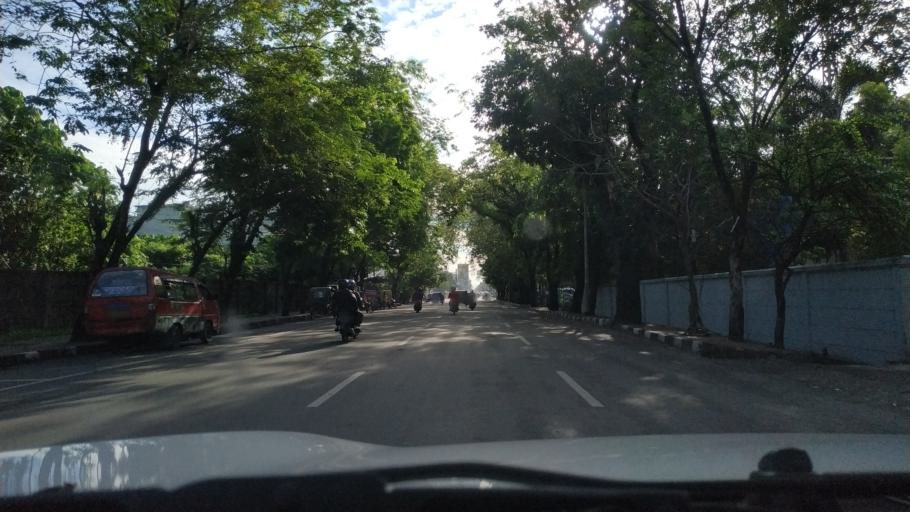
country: ID
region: North Sumatra
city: Medan
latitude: 3.5987
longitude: 98.6892
